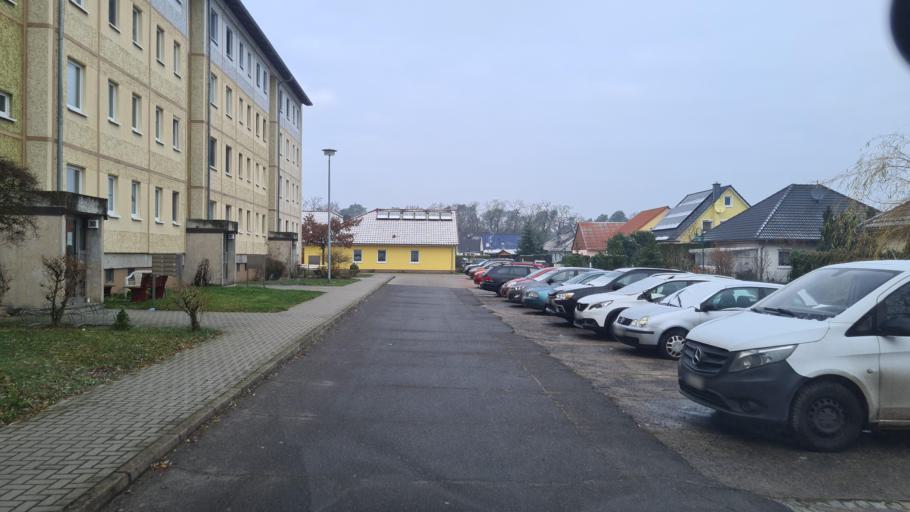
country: DE
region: Brandenburg
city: Spreenhagen
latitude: 52.3468
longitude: 13.8746
